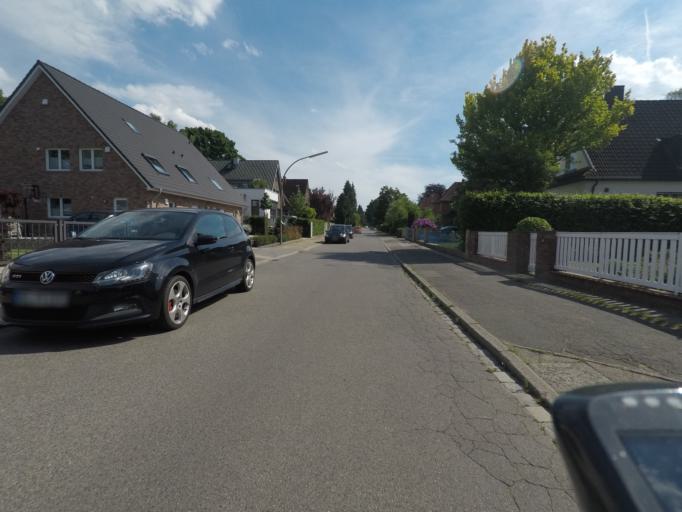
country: DE
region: Schleswig-Holstein
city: Barsbuettel
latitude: 53.6095
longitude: 10.1676
